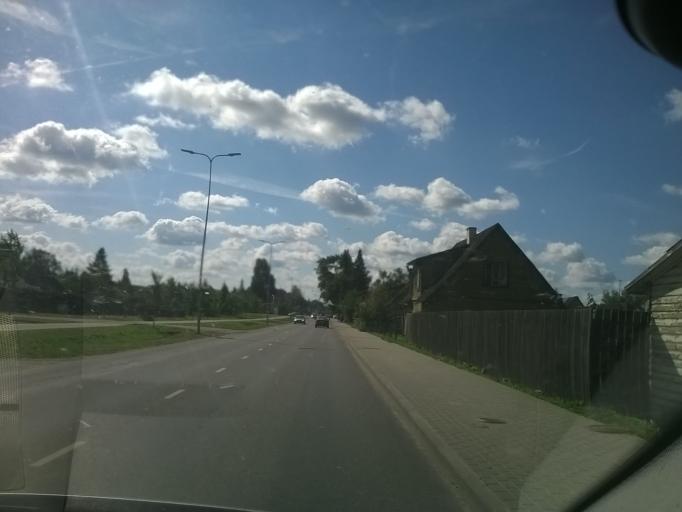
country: EE
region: Vorumaa
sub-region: Voru linn
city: Voru
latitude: 57.8408
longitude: 27.0067
